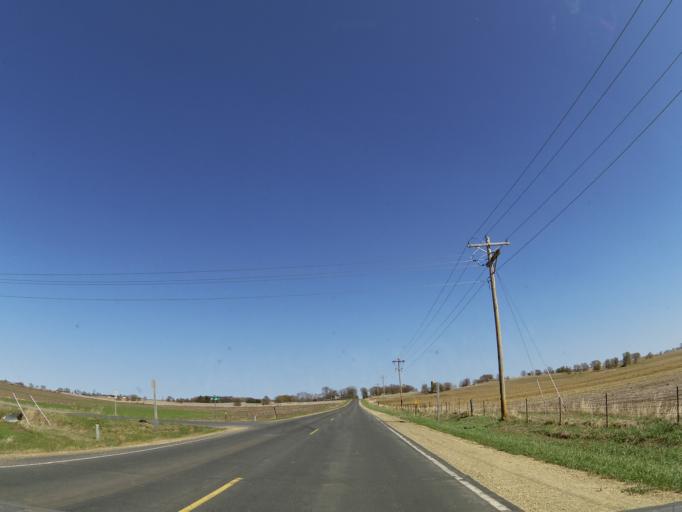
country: US
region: Wisconsin
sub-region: Saint Croix County
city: Roberts
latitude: 44.9351
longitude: -92.5181
